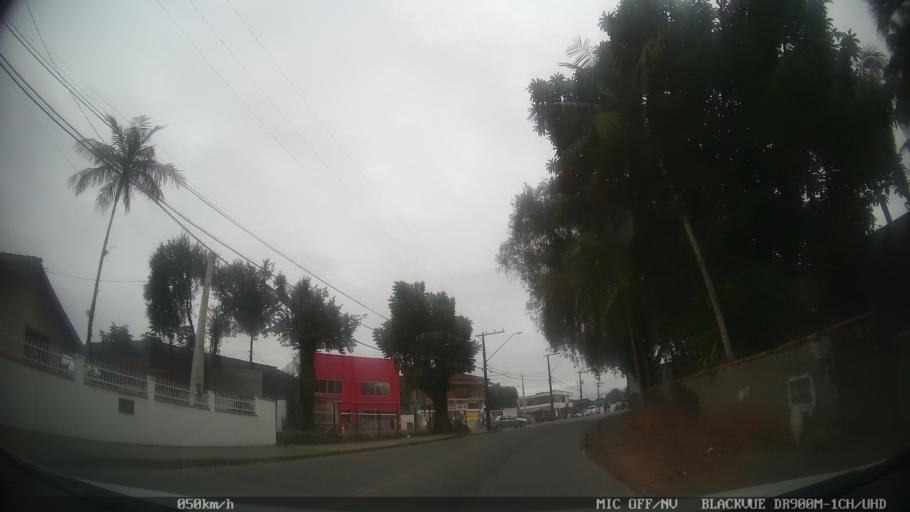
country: BR
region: Santa Catarina
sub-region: Joinville
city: Joinville
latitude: -26.3297
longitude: -48.8110
